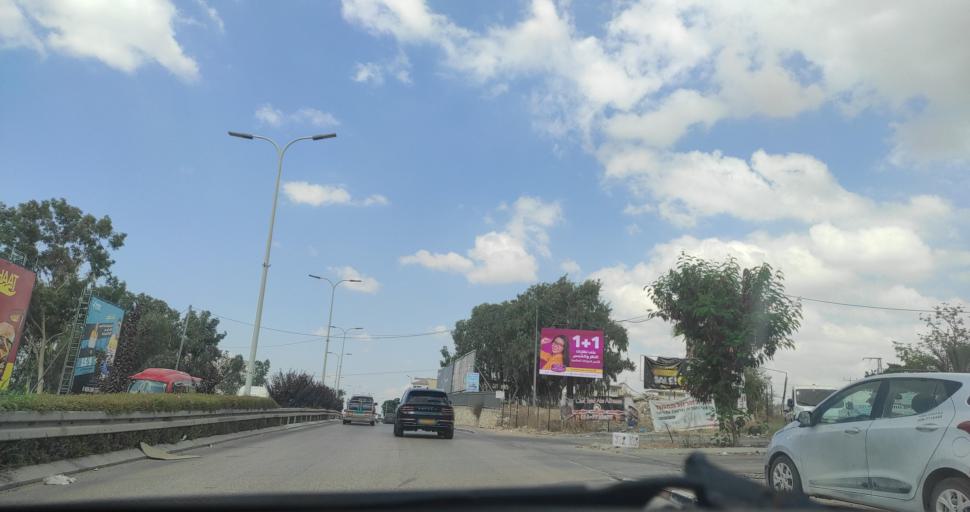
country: IL
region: Central District
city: Kafr Qasim
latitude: 32.1163
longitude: 34.9639
